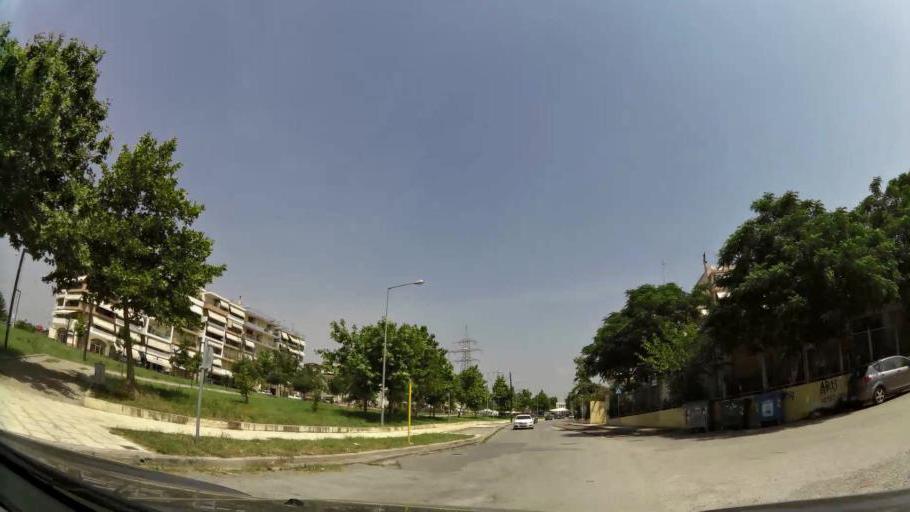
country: GR
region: Central Macedonia
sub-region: Nomos Thessalonikis
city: Evosmos
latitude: 40.6726
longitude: 22.9030
